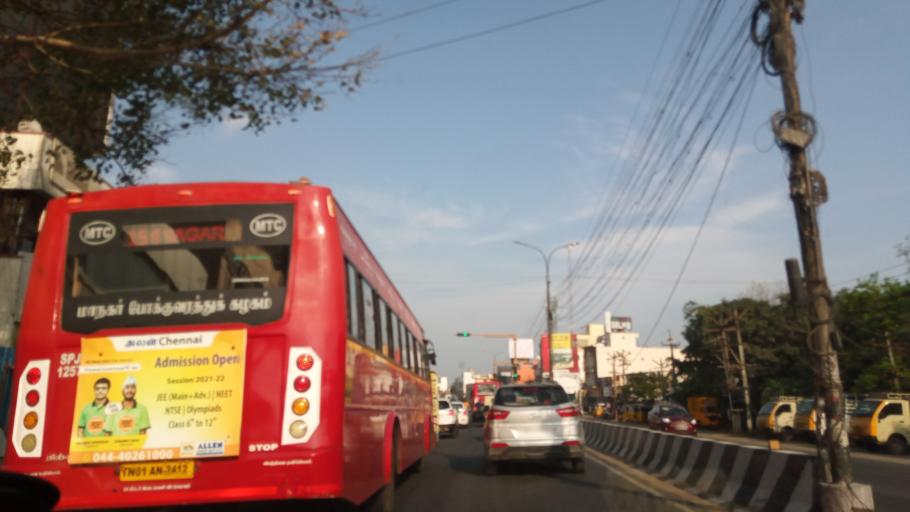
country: IN
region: Tamil Nadu
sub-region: Kancheepuram
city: Poonamalle
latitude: 13.0384
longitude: 80.1346
